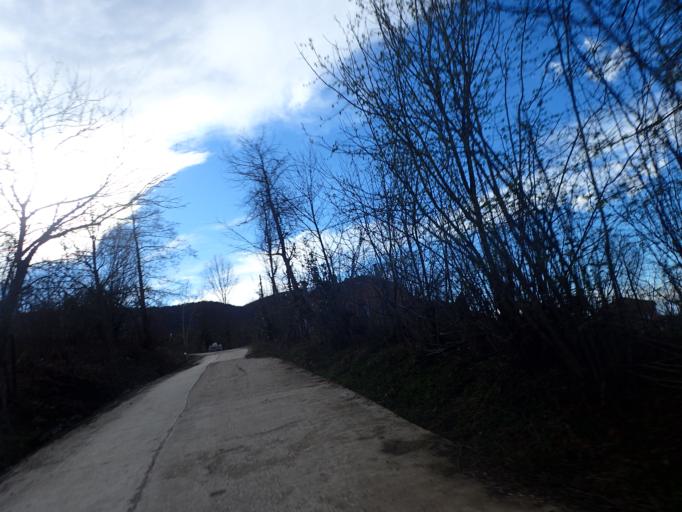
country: TR
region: Ordu
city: Kumru
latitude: 40.9284
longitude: 37.2483
